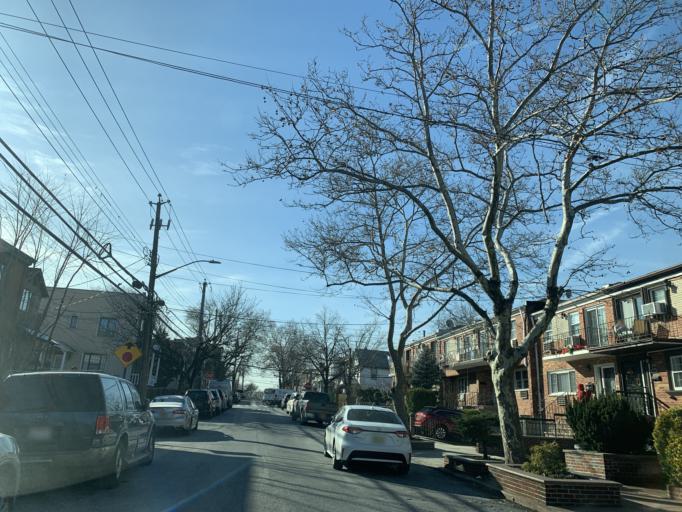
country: US
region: New York
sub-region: Kings County
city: East New York
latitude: 40.7246
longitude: -73.8911
